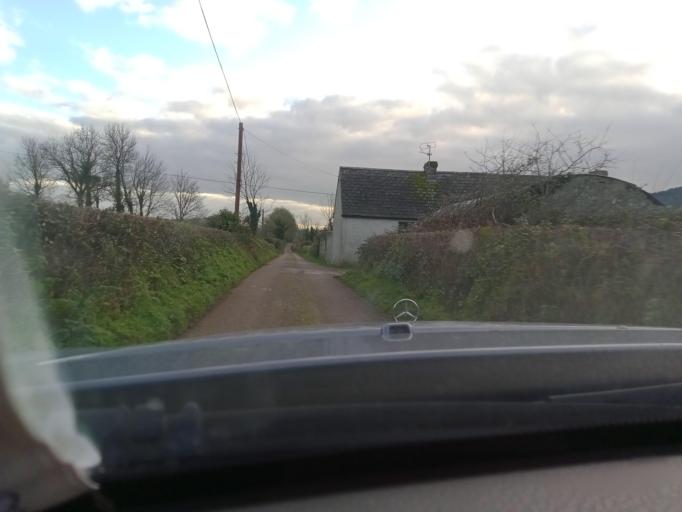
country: IE
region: Leinster
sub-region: Kilkenny
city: Graiguenamanagh
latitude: 52.5166
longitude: -6.9443
